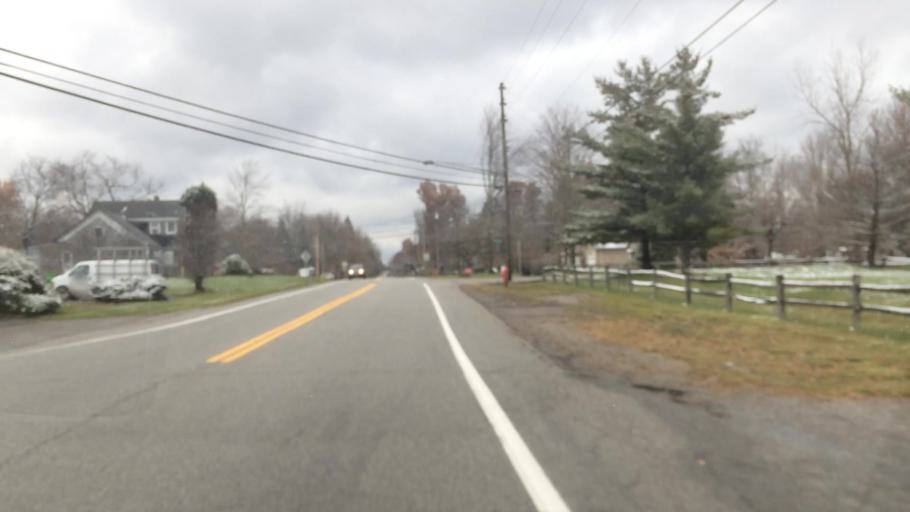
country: US
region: Ohio
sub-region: Summit County
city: Macedonia
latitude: 41.2949
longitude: -81.5233
